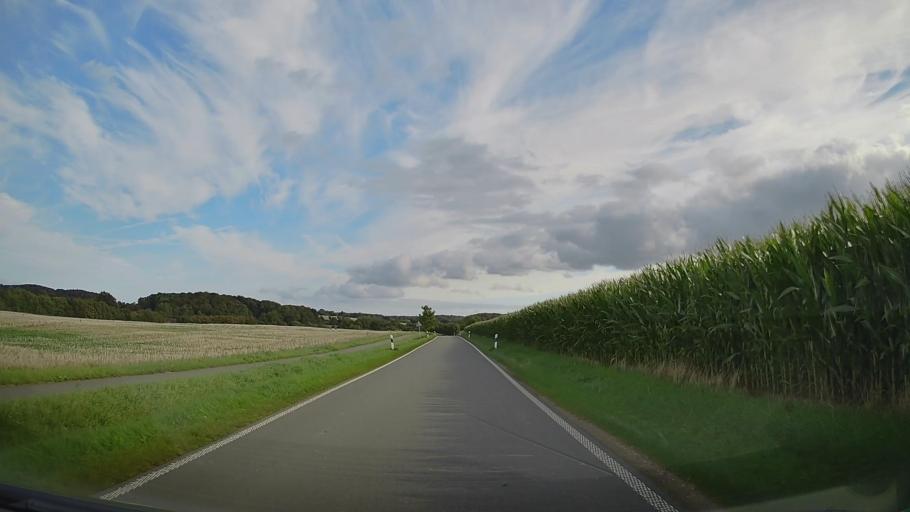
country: DE
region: Schleswig-Holstein
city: Westerholz
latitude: 54.8084
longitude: 9.6807
